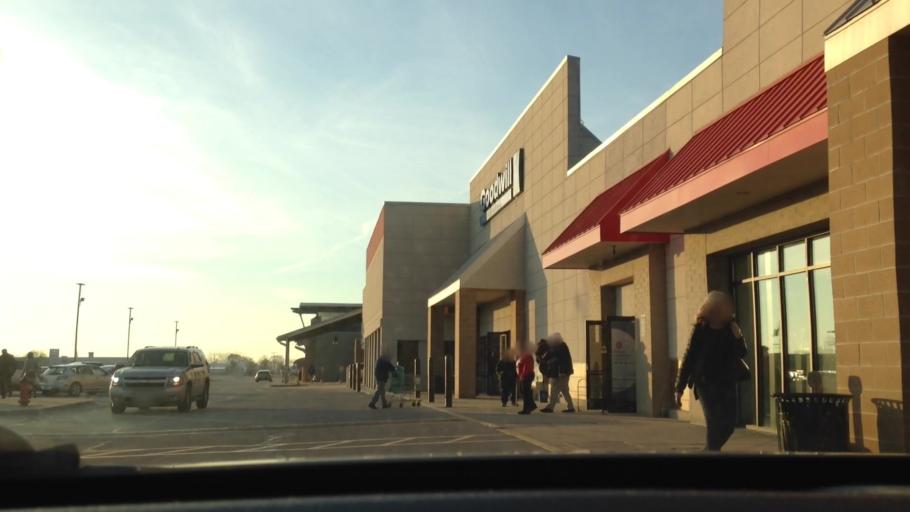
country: US
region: Missouri
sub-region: Clay County
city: Gladstone
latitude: 39.1825
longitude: -94.5774
